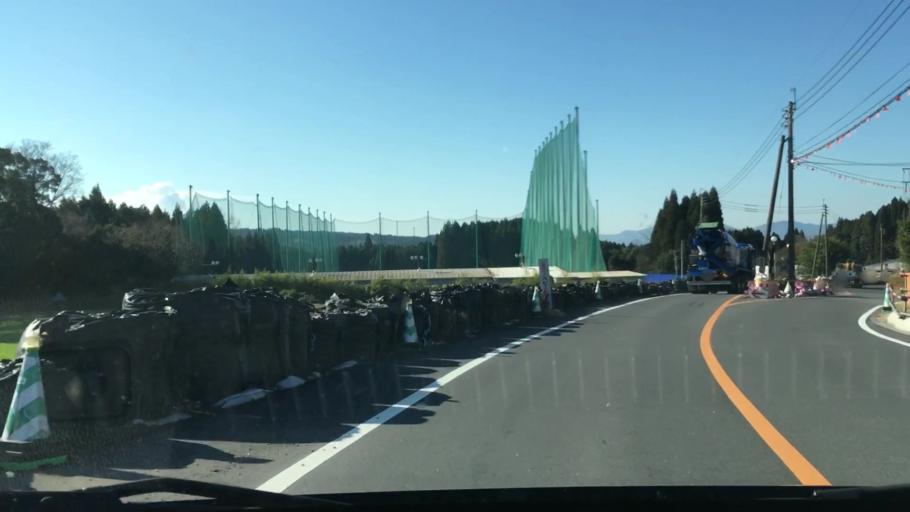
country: JP
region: Kagoshima
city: Kajiki
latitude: 31.7737
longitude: 130.7000
